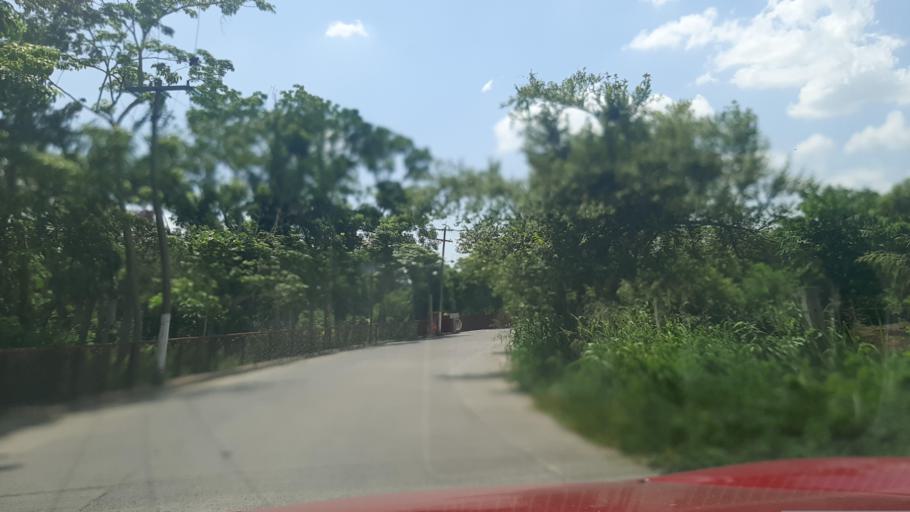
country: MX
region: Veracruz
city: Coatzintla
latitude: 20.4976
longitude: -97.4372
